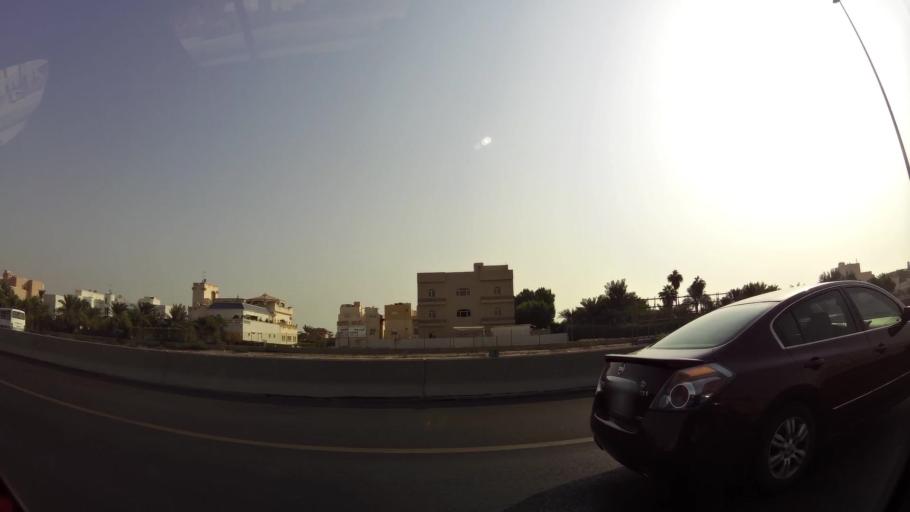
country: KW
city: Al Funaytis
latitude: 29.2232
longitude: 48.0998
